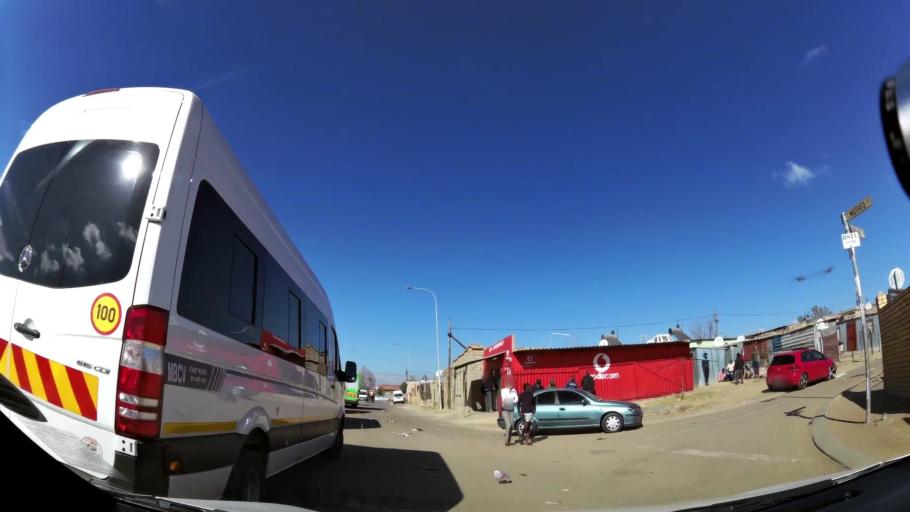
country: ZA
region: Gauteng
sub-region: City of Johannesburg Metropolitan Municipality
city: Midrand
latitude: -25.9140
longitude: 28.0943
